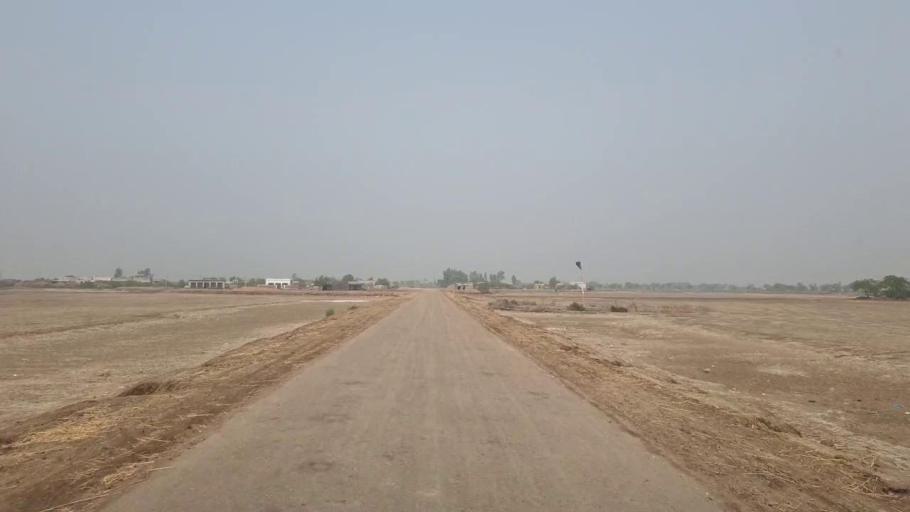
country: PK
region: Sindh
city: Kario
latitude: 24.6566
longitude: 68.6213
